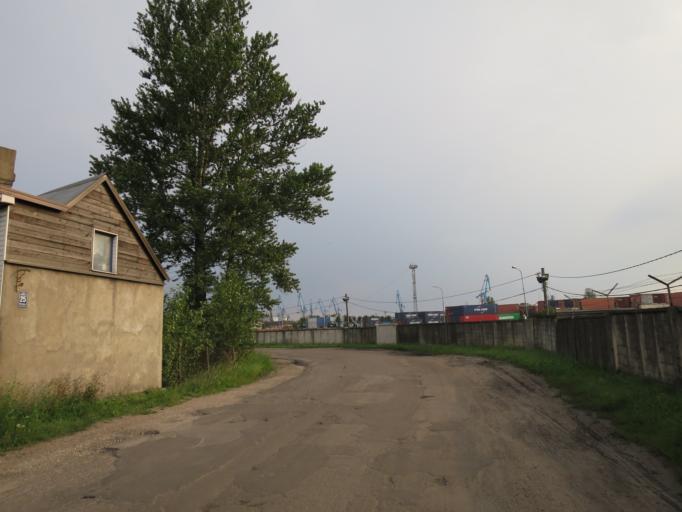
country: LV
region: Riga
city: Riga
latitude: 56.9799
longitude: 24.0991
